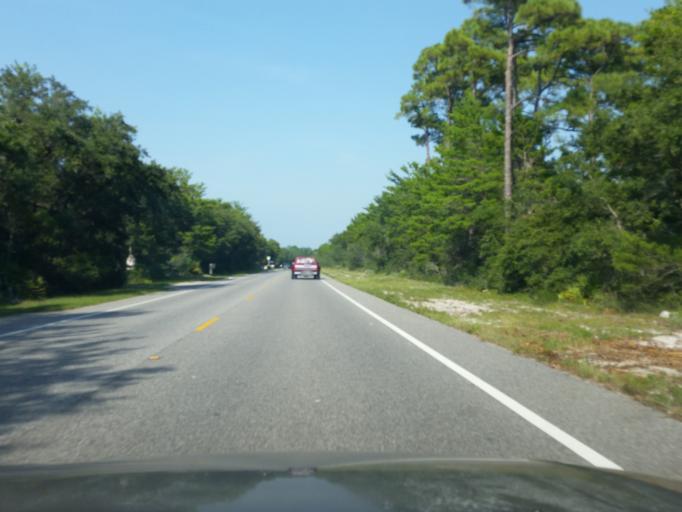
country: US
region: Alabama
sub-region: Baldwin County
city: Gulf Shores
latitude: 30.2454
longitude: -87.8368
